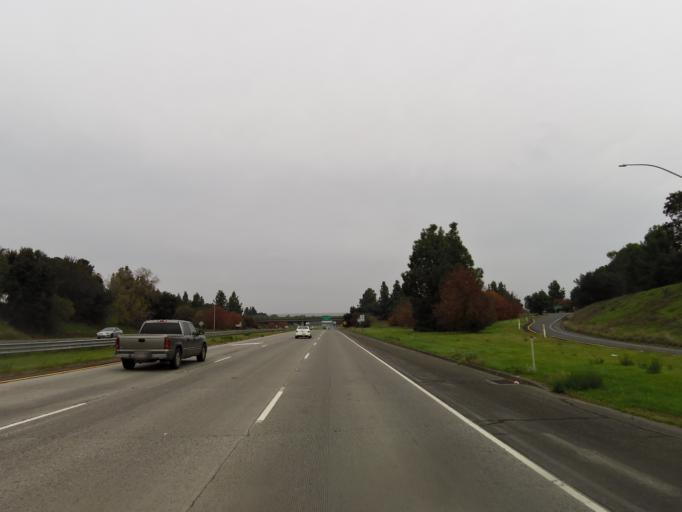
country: US
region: California
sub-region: Yolo County
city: Davis
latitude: 38.5340
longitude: -121.7684
